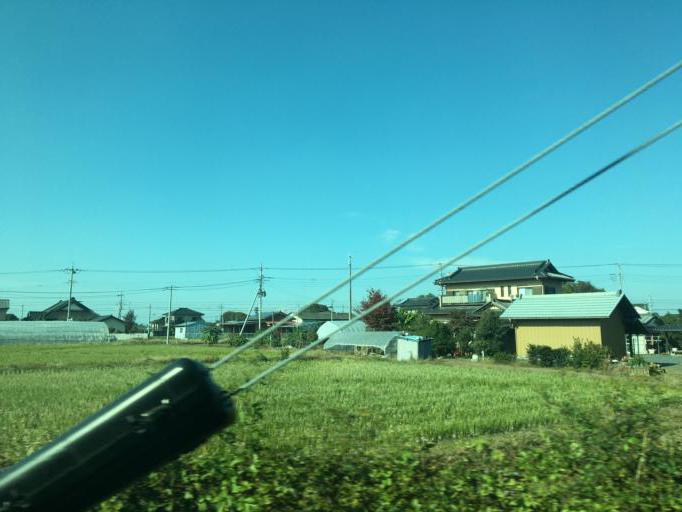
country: JP
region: Ibaraki
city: Shimodate
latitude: 36.3255
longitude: 140.0343
